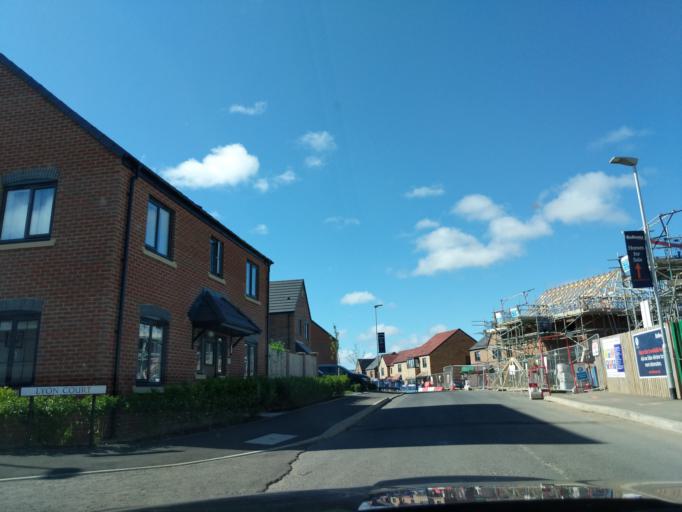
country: GB
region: England
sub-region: Northumberland
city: Newbiggin-by-the-Sea
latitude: 55.1707
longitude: -1.5455
